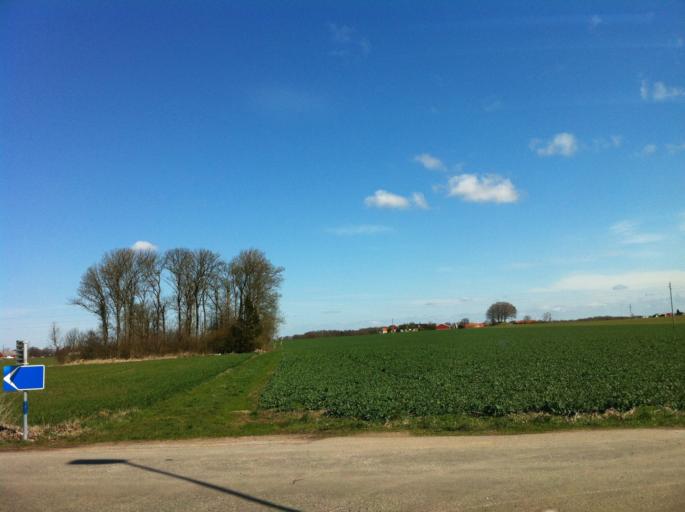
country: SE
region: Skane
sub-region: Helsingborg
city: Glumslov
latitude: 55.9580
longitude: 12.8344
